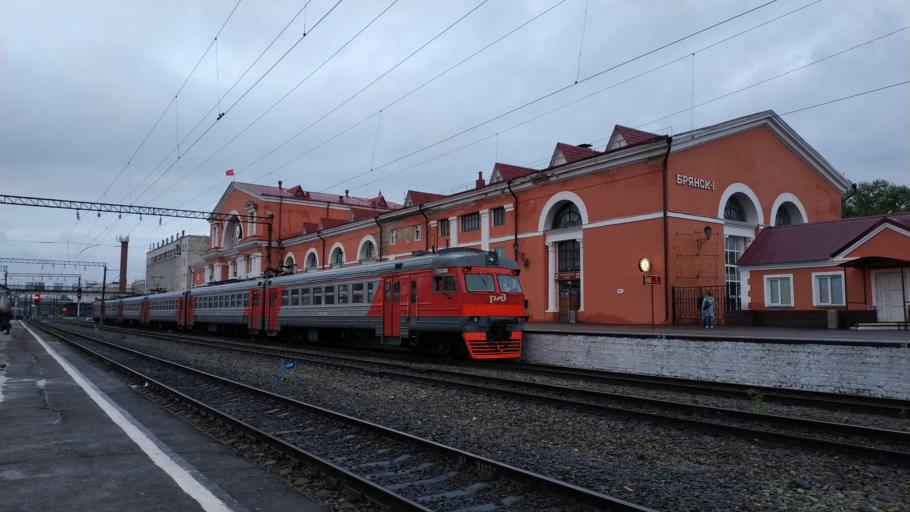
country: RU
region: Brjansk
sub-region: Bryanskiy Rayon
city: Bryansk
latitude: 53.2631
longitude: 34.4055
